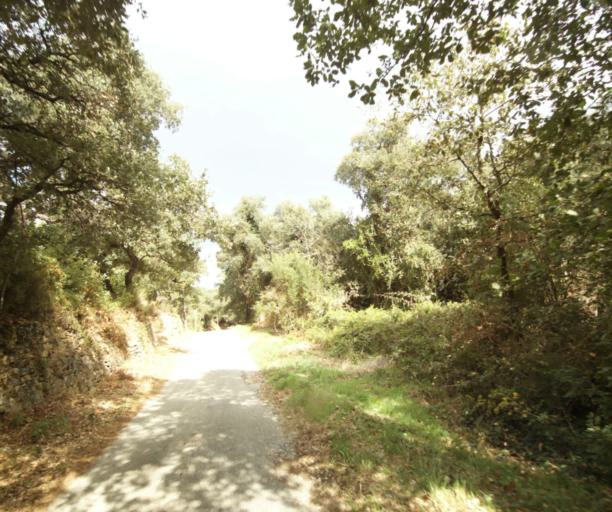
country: FR
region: Languedoc-Roussillon
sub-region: Departement des Pyrenees-Orientales
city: Argelers
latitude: 42.5387
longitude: 3.0100
